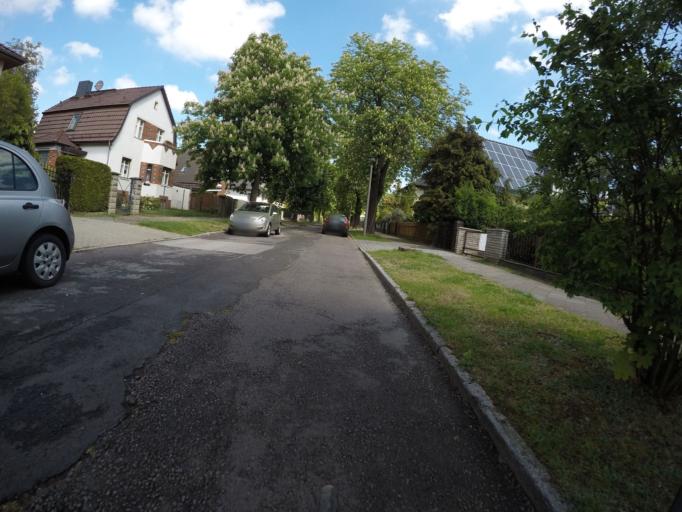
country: DE
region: Berlin
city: Biesdorf
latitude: 52.5141
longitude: 13.5506
